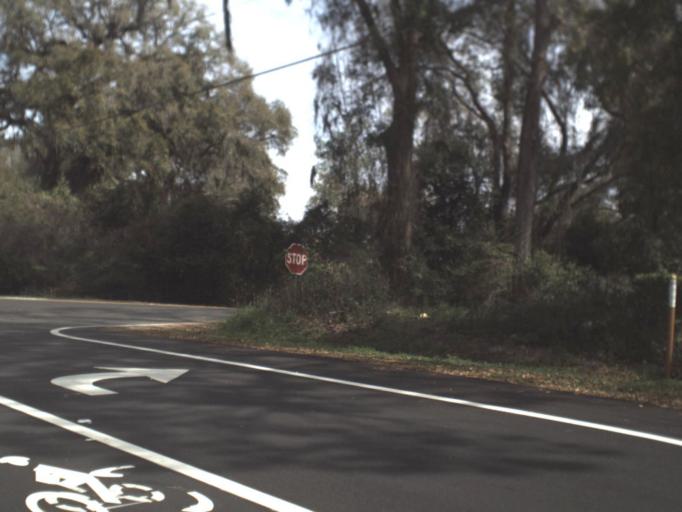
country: US
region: Florida
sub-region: Gadsden County
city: Midway
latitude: 30.5249
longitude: -84.3632
